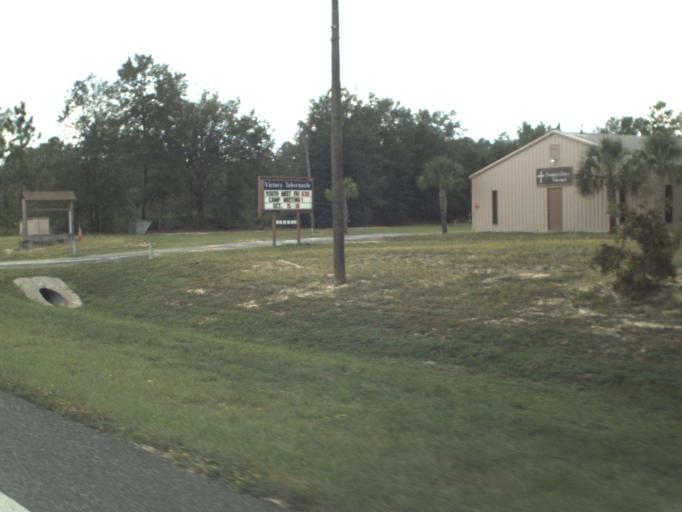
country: US
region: Florida
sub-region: Bay County
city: Youngstown
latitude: 30.4893
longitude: -85.4177
